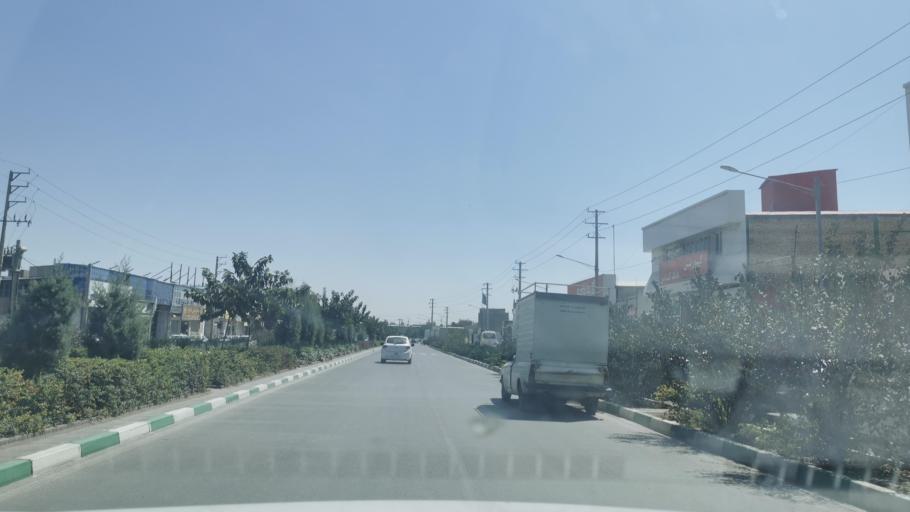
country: IR
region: Razavi Khorasan
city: Mashhad
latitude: 36.3520
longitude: 59.5731
